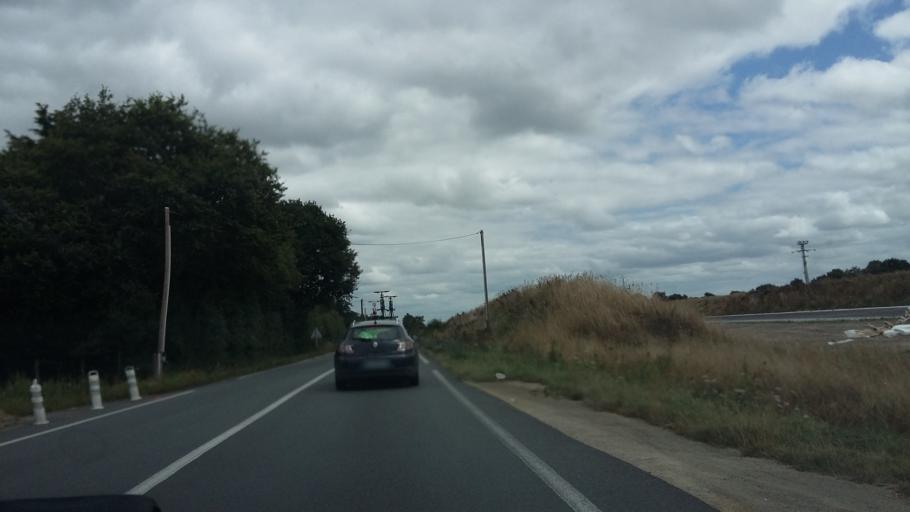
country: FR
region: Pays de la Loire
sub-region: Departement de la Vendee
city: Challans
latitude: 46.8351
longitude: -1.8331
